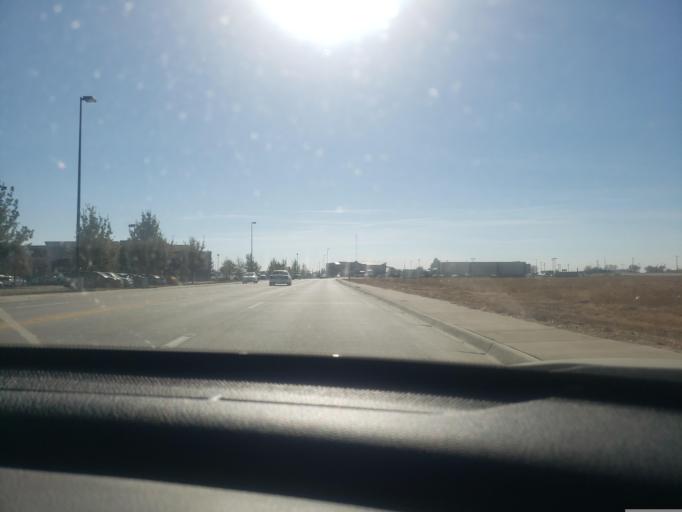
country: US
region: Kansas
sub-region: Finney County
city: Garden City
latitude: 37.9794
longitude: -100.8367
